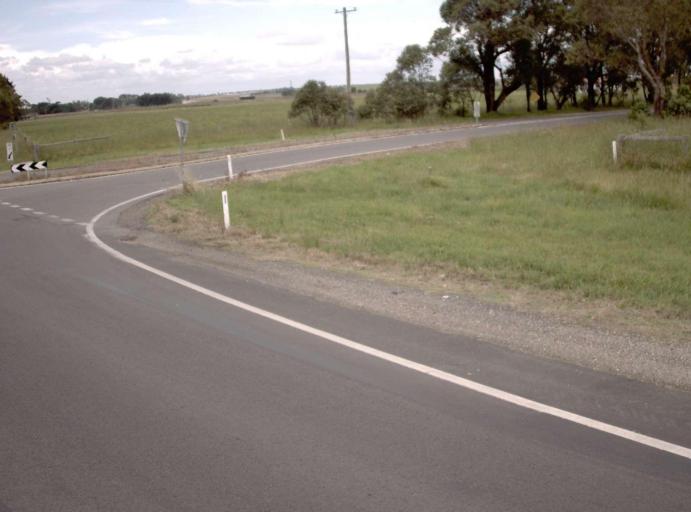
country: AU
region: Victoria
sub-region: Wellington
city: Sale
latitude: -37.9817
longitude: 147.0720
